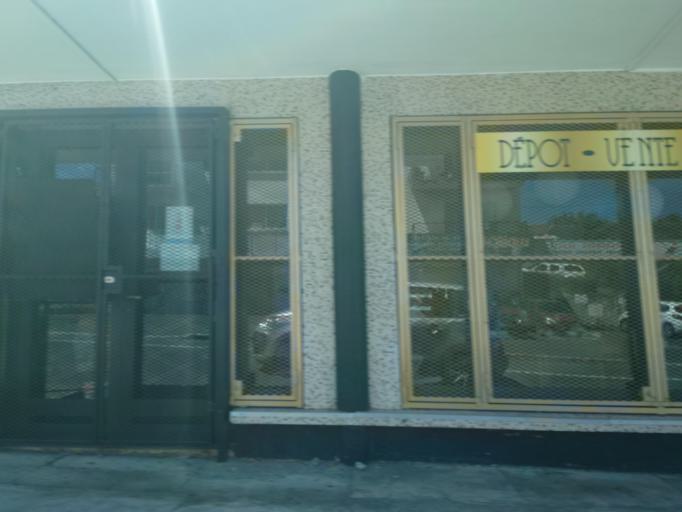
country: NC
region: South Province
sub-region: Noumea
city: Noumea
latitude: -22.2700
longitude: 166.4544
